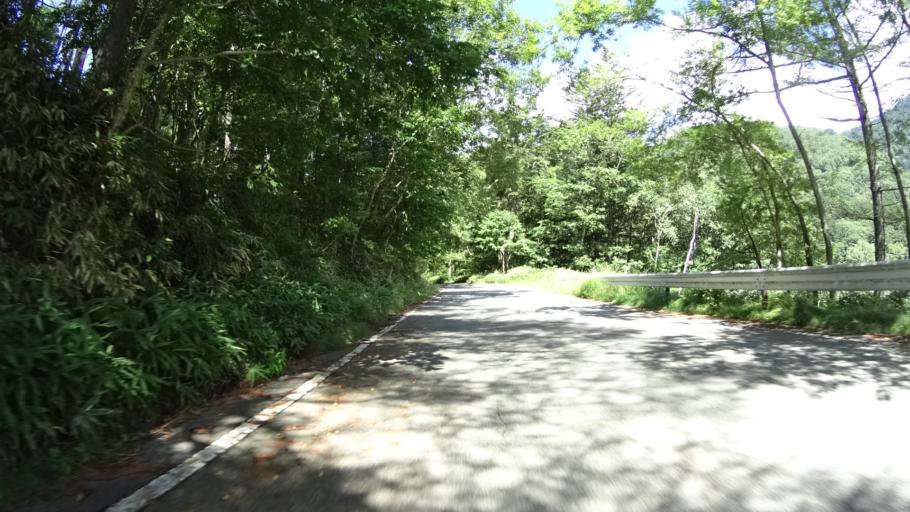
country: JP
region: Yamanashi
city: Enzan
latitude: 35.7314
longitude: 138.8404
